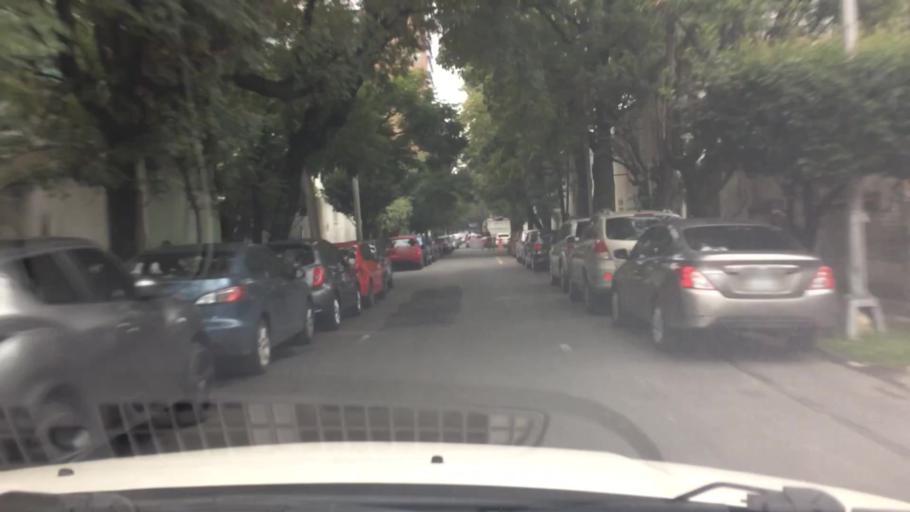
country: MX
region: Mexico City
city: Alvaro Obregon
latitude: 19.3536
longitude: -99.1874
